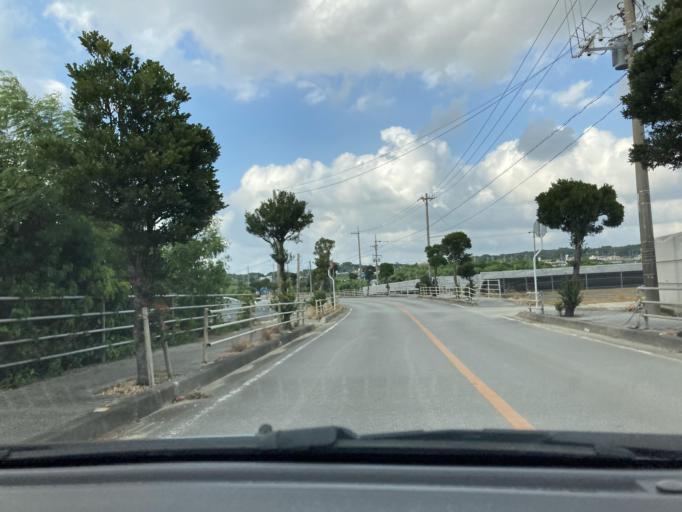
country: JP
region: Okinawa
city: Itoman
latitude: 26.0986
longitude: 127.6656
